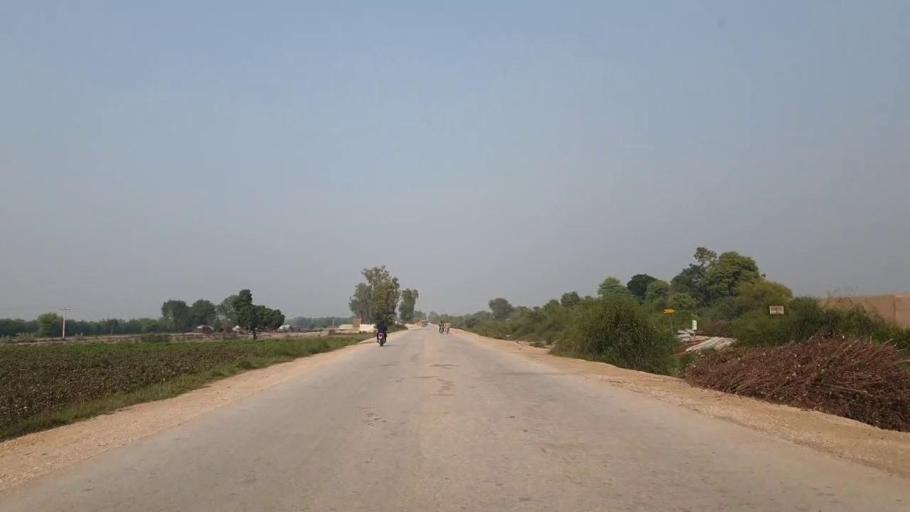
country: PK
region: Sindh
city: Bhan
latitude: 26.5789
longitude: 67.7282
